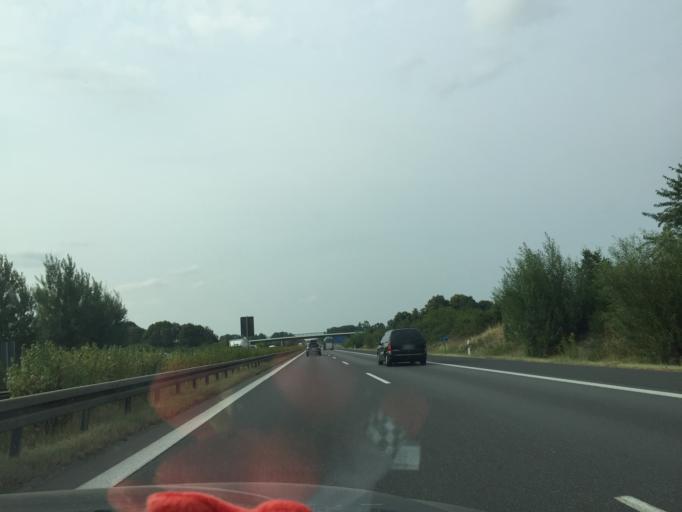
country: DE
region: Brandenburg
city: Mittenwalde
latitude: 52.2709
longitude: 13.5733
